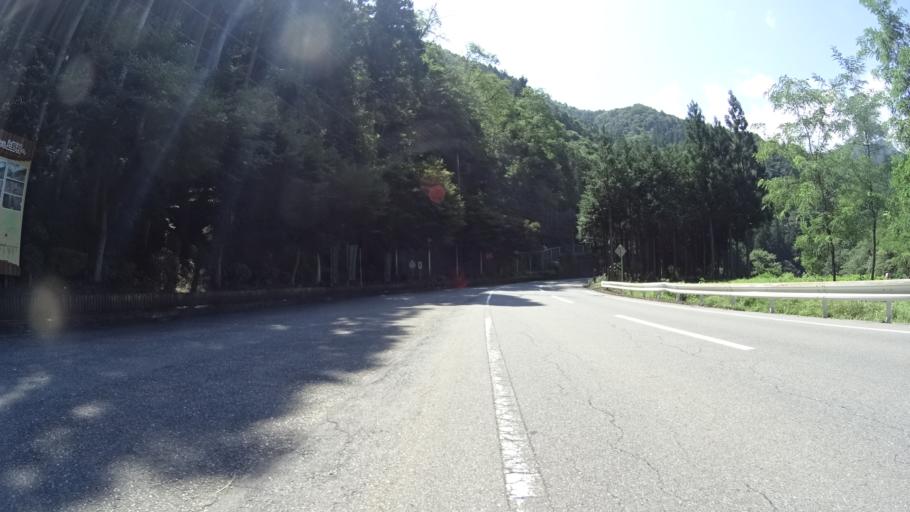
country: JP
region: Gunma
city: Tomioka
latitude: 36.0852
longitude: 138.8030
